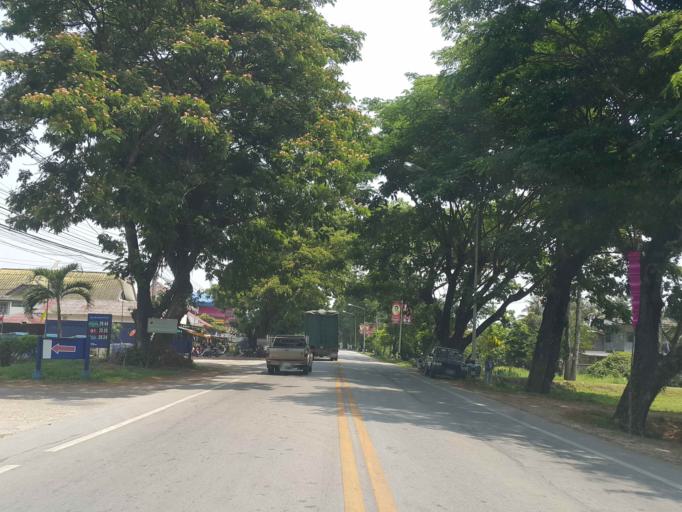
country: TH
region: Chiang Mai
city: Mae Taeng
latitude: 19.0376
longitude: 98.9690
